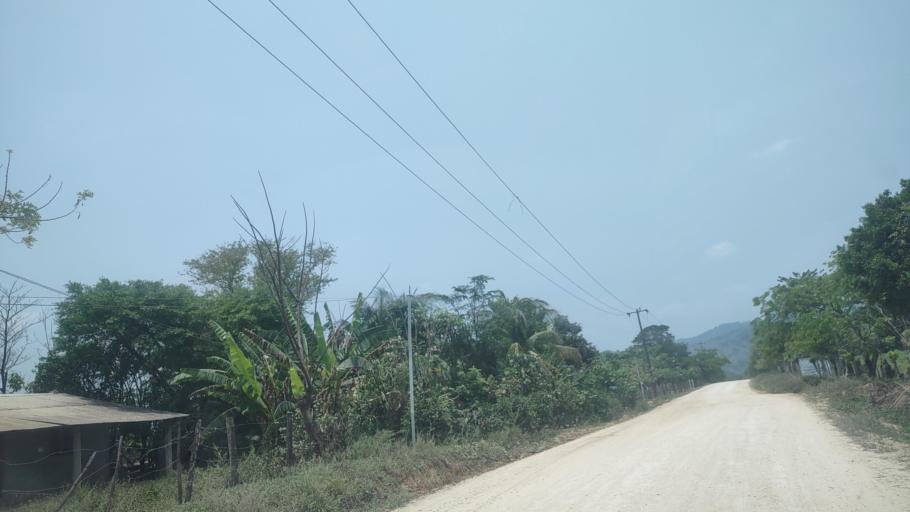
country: MX
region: Chiapas
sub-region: Tecpatan
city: Raudales Malpaso
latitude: 17.4594
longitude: -93.8051
